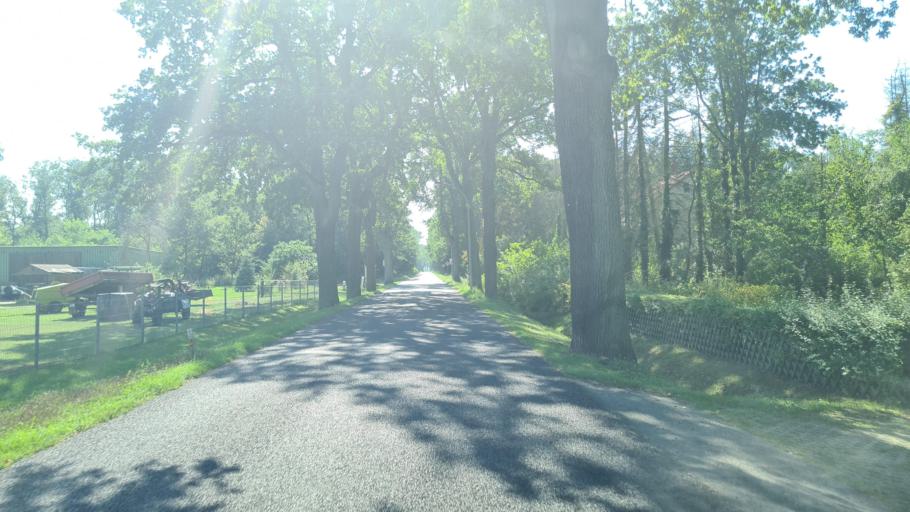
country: DE
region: Brandenburg
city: Paulinenaue
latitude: 52.6638
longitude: 12.7113
